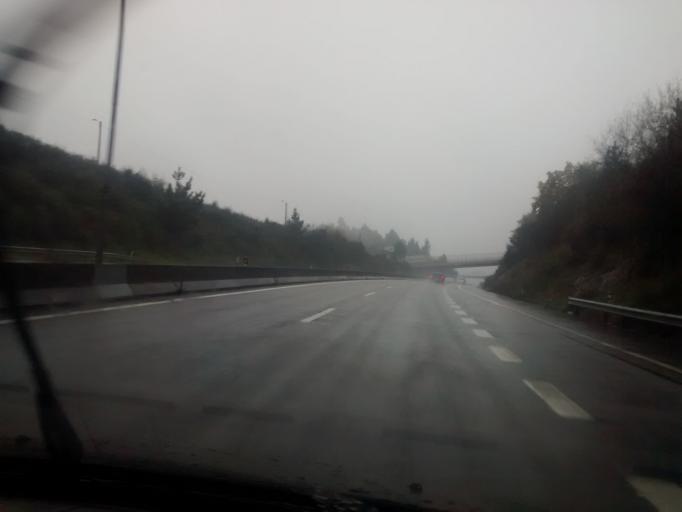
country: PT
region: Braga
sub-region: Braga
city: Braga
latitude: 41.5271
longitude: -8.4442
